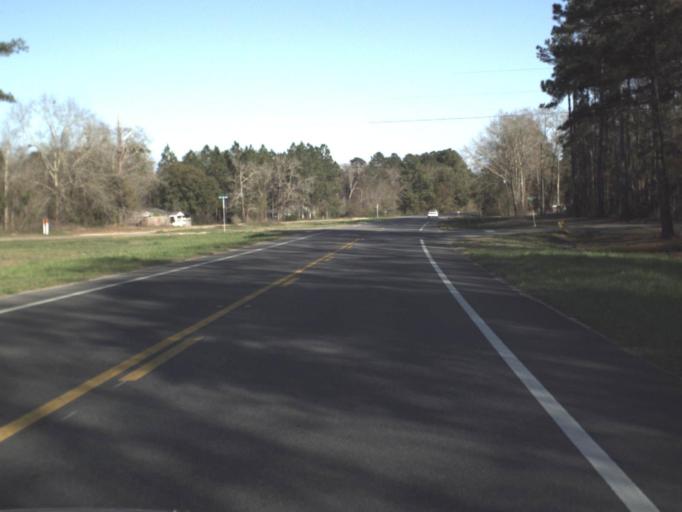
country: US
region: Florida
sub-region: Jackson County
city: Sneads
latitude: 30.7184
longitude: -84.9639
